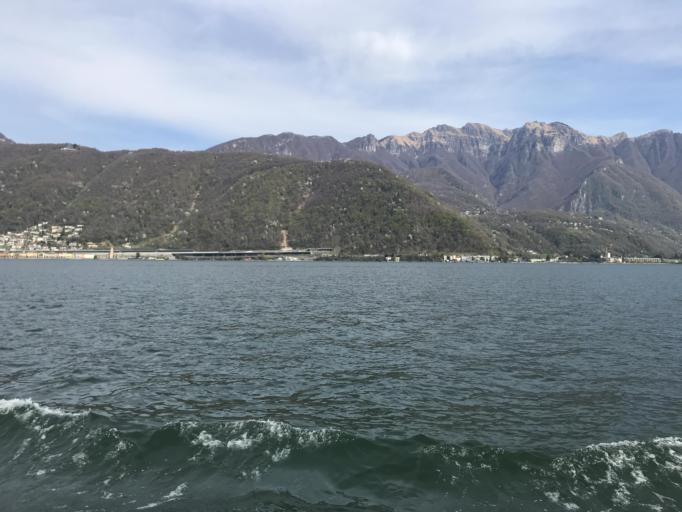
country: CH
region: Ticino
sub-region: Lugano District
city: Melide
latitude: 45.9435
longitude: 8.9464
